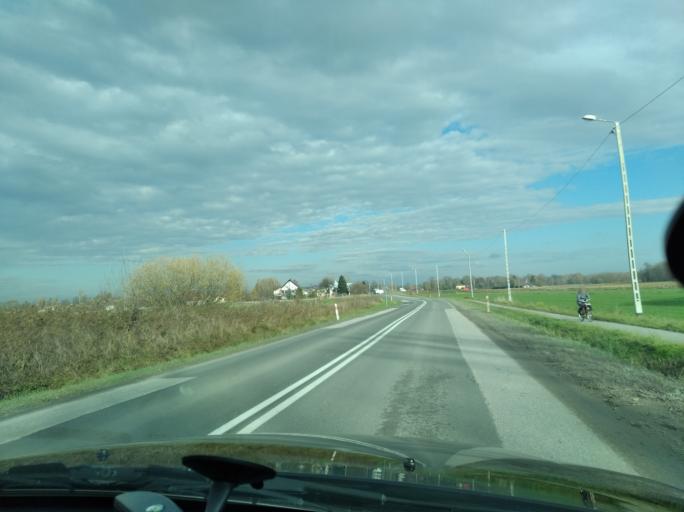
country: PL
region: Subcarpathian Voivodeship
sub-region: Powiat ropczycko-sedziszowski
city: Ostrow
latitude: 50.0894
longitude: 21.5910
